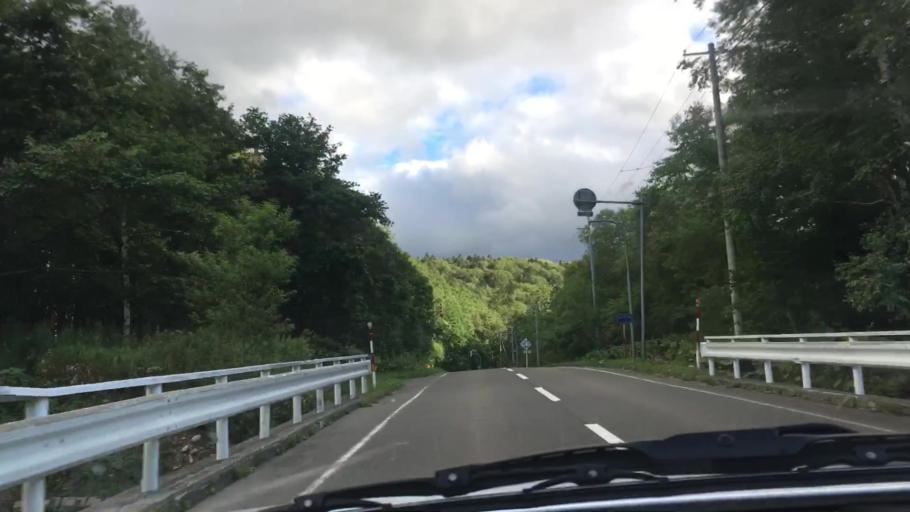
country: JP
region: Hokkaido
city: Shimo-furano
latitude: 43.0988
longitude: 142.6851
